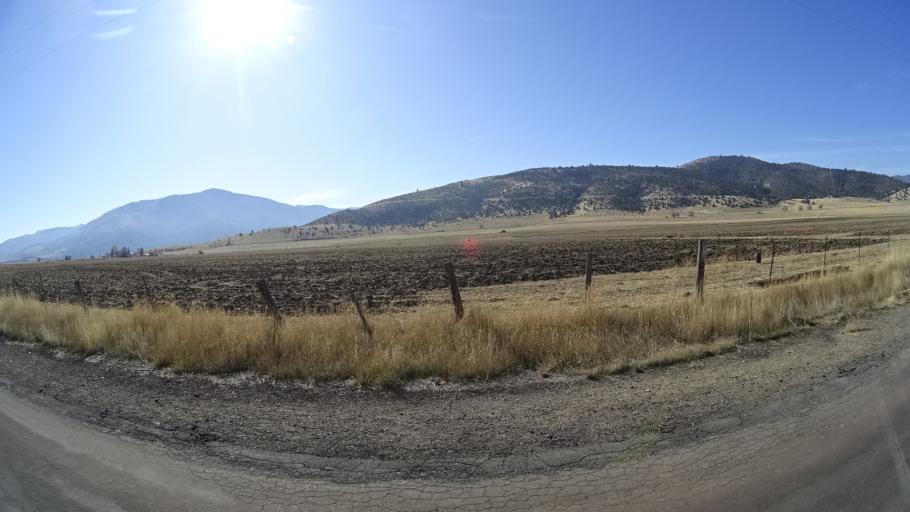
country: US
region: California
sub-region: Siskiyou County
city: Weed
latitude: 41.5230
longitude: -122.5271
